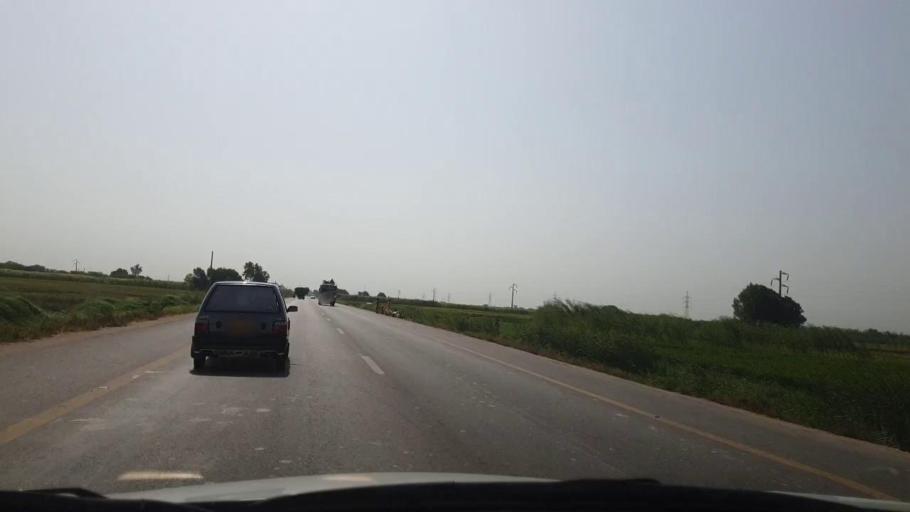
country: PK
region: Sindh
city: Tando Muhammad Khan
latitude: 25.1124
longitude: 68.5787
